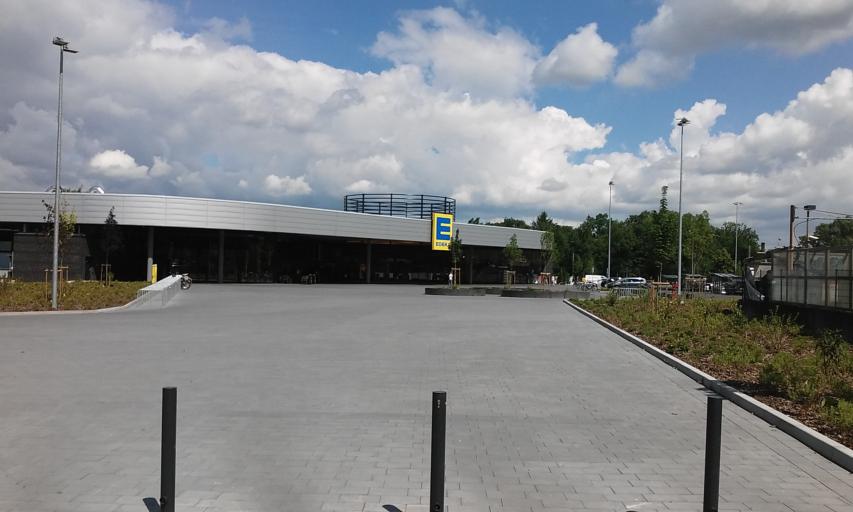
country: DE
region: Lower Saxony
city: Goettingen
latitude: 51.5336
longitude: 9.9076
